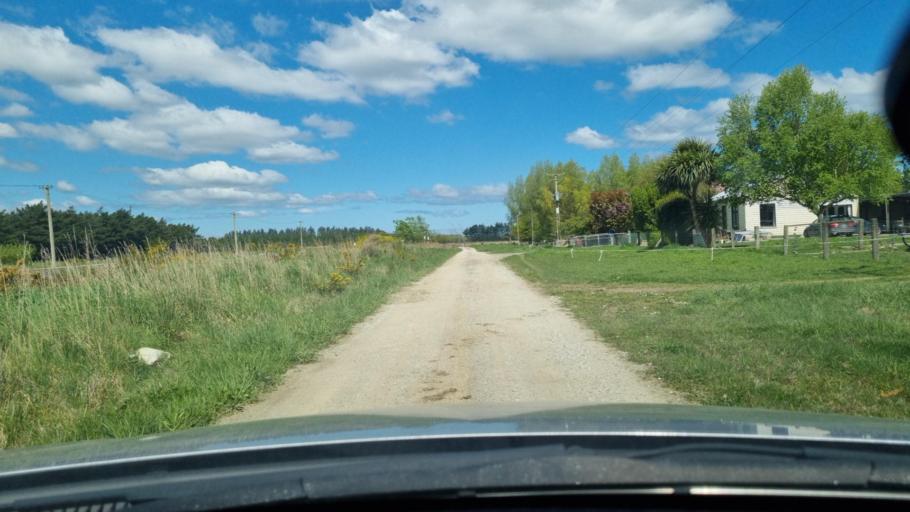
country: NZ
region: Southland
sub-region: Invercargill City
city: Invercargill
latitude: -46.3479
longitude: 168.3400
